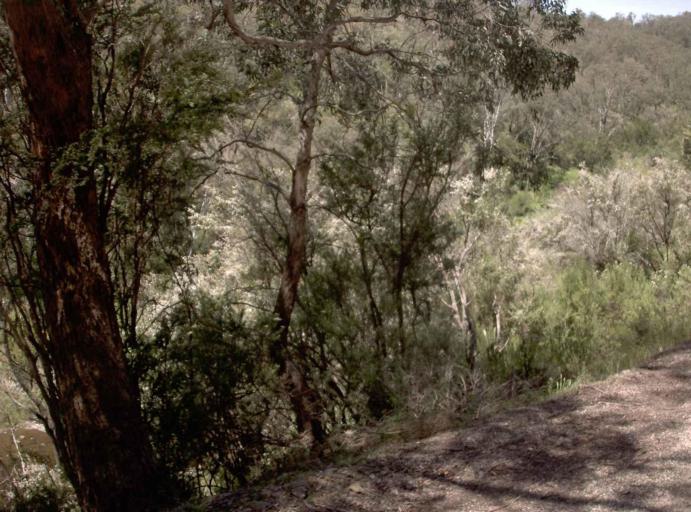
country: AU
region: Victoria
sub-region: East Gippsland
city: Bairnsdale
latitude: -37.4526
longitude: 147.8276
